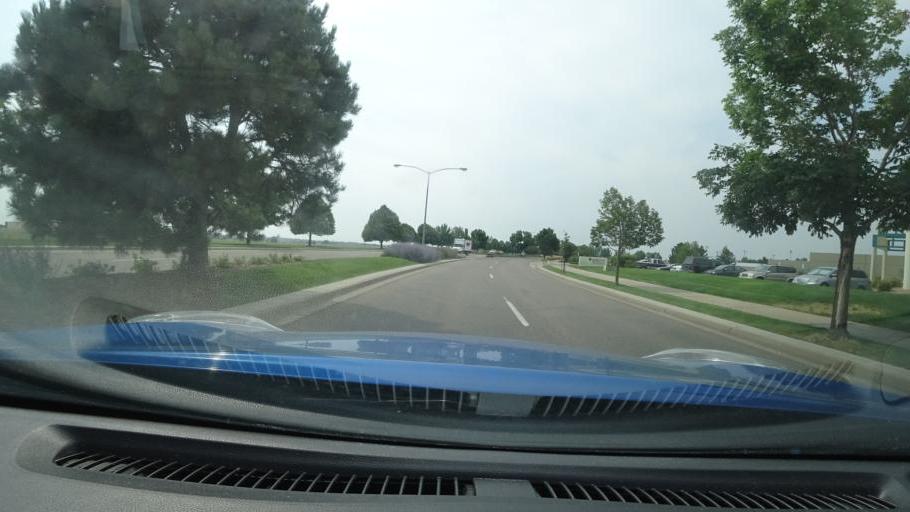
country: US
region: Colorado
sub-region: Adams County
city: Aurora
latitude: 39.7591
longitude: -104.7602
